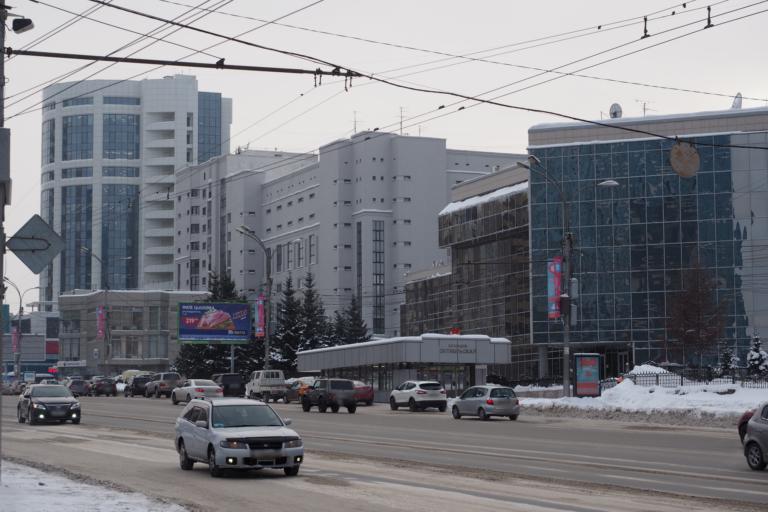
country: RU
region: Novosibirsk
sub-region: Novosibirskiy Rayon
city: Novosibirsk
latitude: 55.0201
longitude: 82.9368
